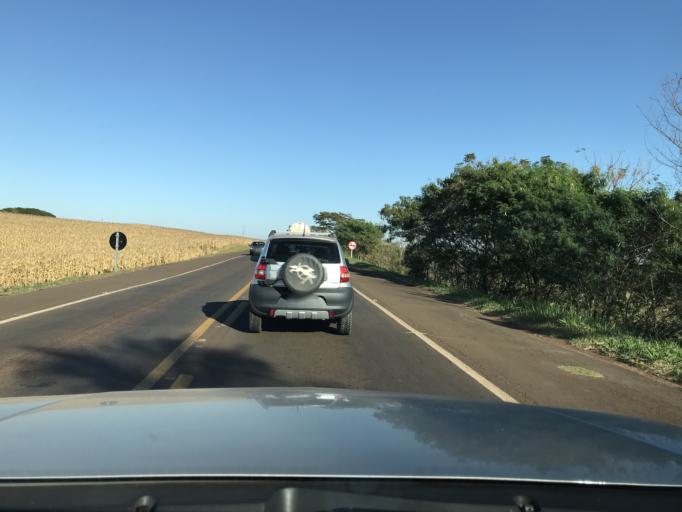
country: BR
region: Parana
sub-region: Ipora
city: Ipora
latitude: -24.0524
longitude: -53.7895
